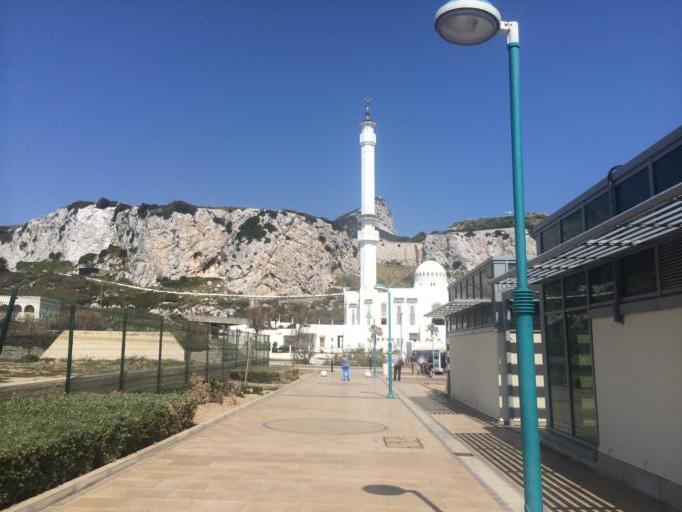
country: GI
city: Gibraltar
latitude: 36.1107
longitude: -5.3459
